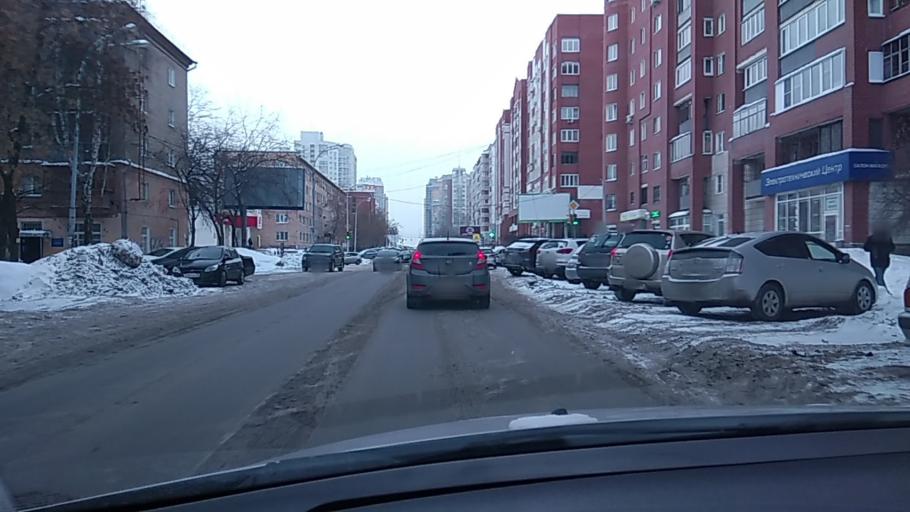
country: RU
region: Sverdlovsk
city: Yekaterinburg
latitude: 56.8107
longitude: 60.6004
